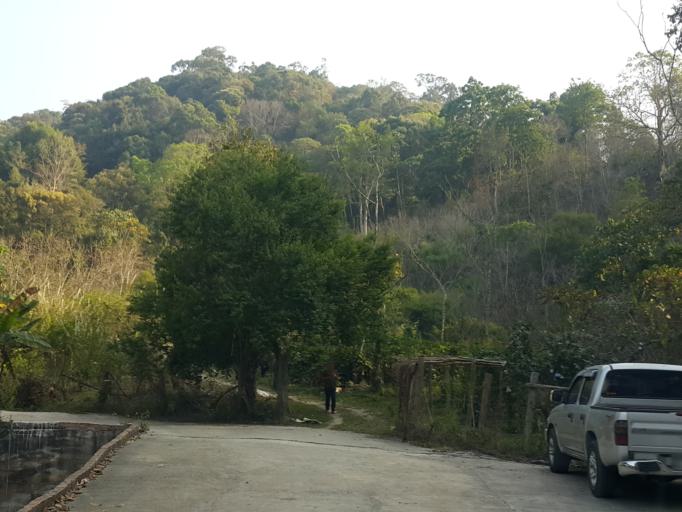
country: TH
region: Chiang Mai
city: Samoeng
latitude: 19.0161
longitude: 98.7615
